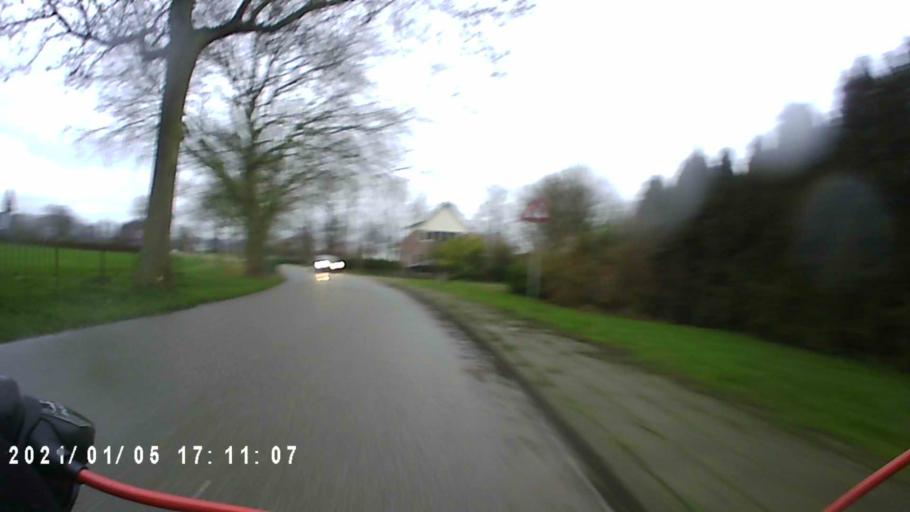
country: NL
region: Groningen
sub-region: Gemeente  Oldambt
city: Winschoten
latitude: 53.2482
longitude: 6.9992
